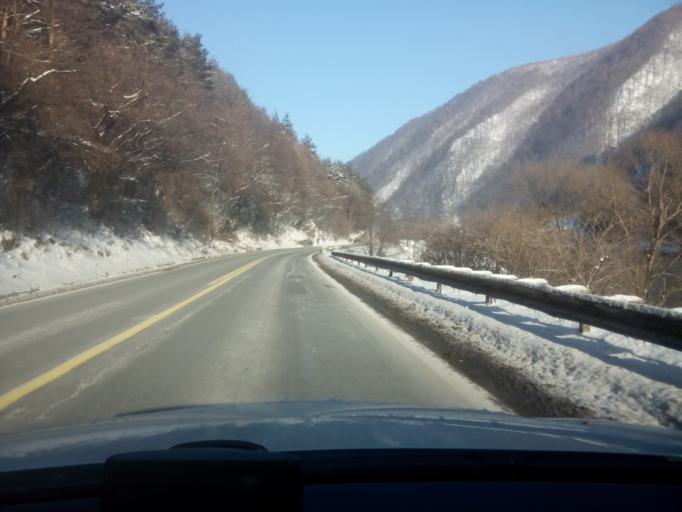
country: RO
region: Sibiu
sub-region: Comuna Boita
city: Boita
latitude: 45.5838
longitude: 24.2534
